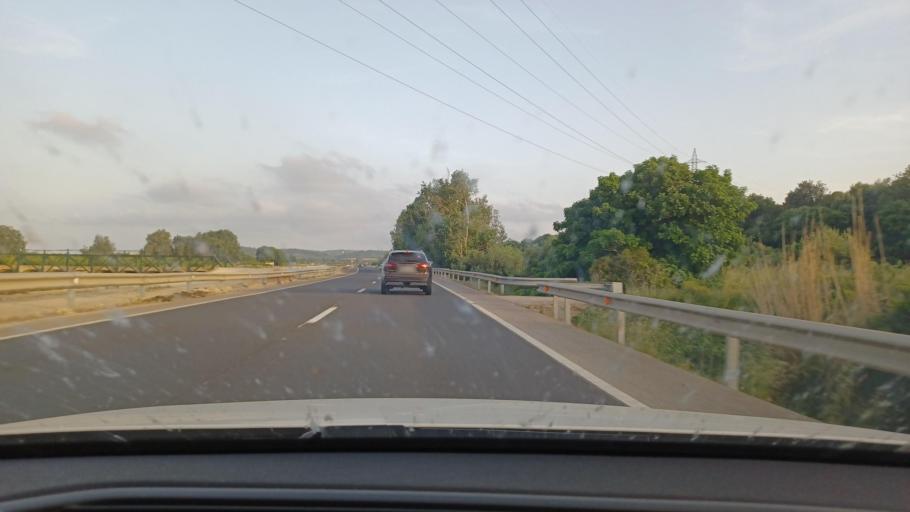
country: ES
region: Catalonia
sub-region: Provincia de Tarragona
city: Masdenverge
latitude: 40.7637
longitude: 0.5329
